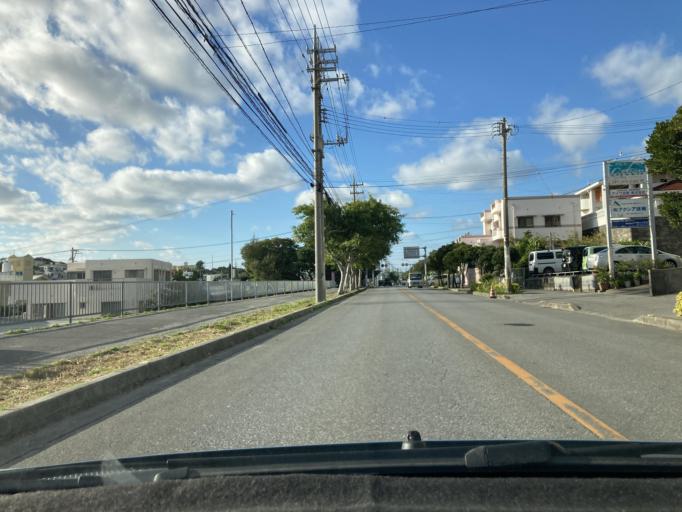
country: JP
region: Okinawa
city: Gushikawa
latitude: 26.3516
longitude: 127.8685
